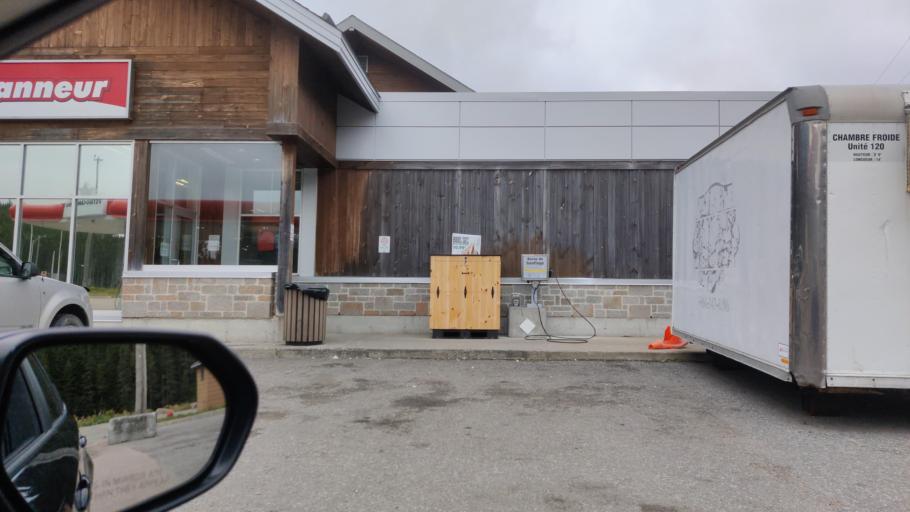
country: CA
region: Quebec
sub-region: Capitale-Nationale
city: Beaupre
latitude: 47.5594
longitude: -71.2307
